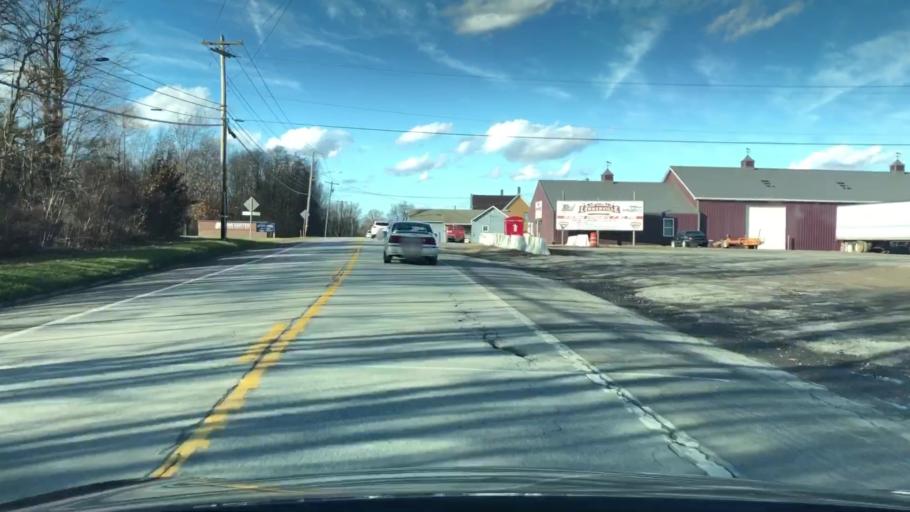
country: US
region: Pennsylvania
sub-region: Butler County
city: Saxonburg
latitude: 40.7378
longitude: -79.7625
